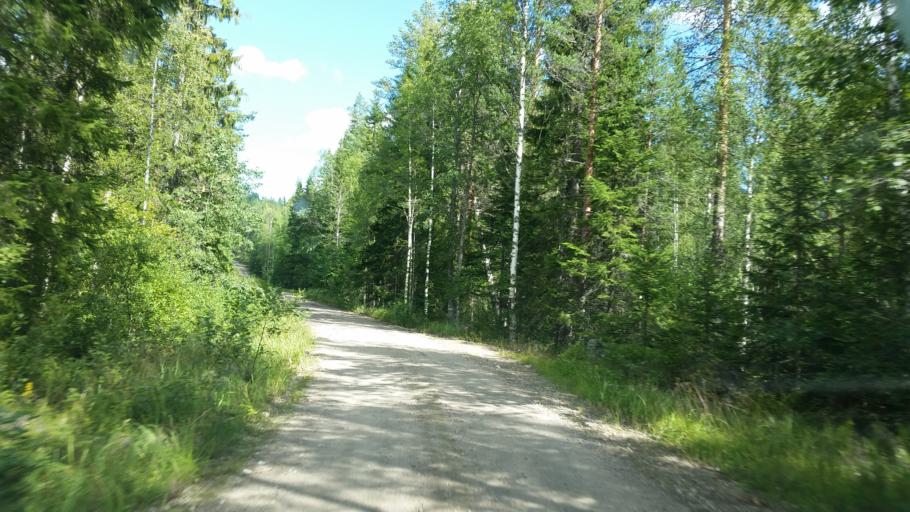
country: SE
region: Gaevleborg
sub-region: Ljusdals Kommun
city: Ljusdal
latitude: 61.9755
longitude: 16.1949
